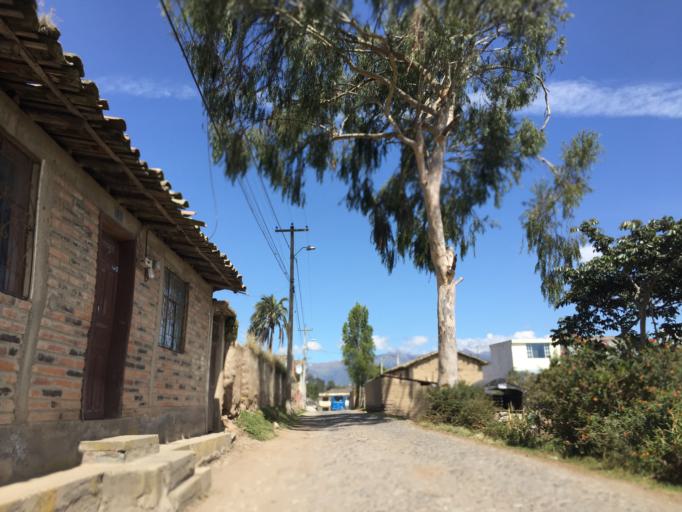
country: EC
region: Imbabura
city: Ibarra
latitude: 0.3144
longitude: -78.1572
